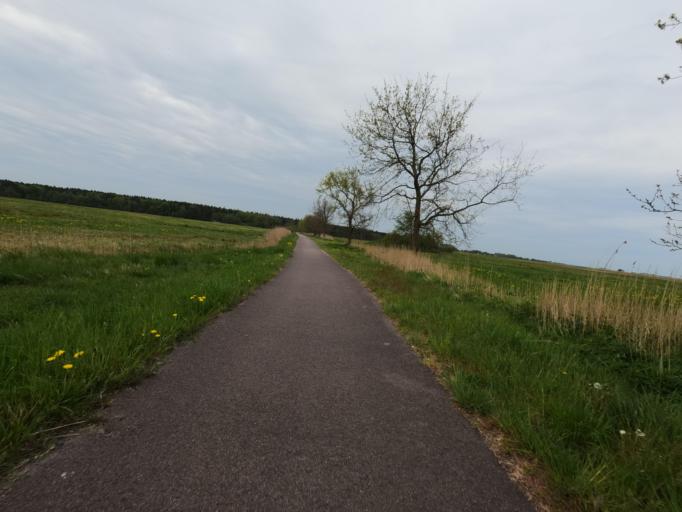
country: DE
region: Mecklenburg-Vorpommern
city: Born
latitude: 54.3561
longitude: 12.5594
